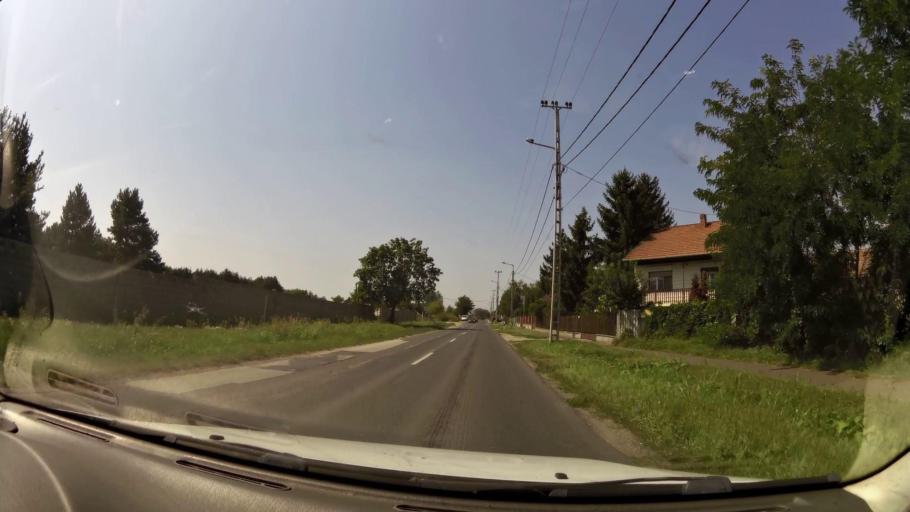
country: HU
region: Pest
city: Tapioszecso
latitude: 47.4479
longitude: 19.5791
